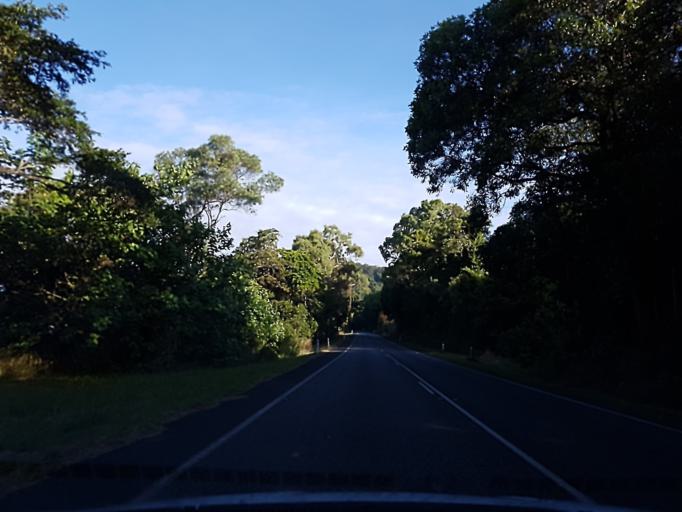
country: AU
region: Queensland
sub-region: Cairns
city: Port Douglas
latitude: -16.3723
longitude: 145.4111
